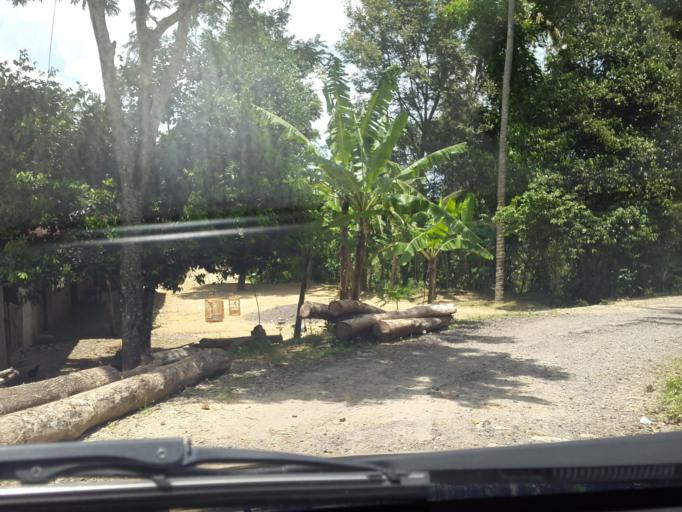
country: ID
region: Daerah Istimewa Yogyakarta
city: Wonosari
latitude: -7.8995
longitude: 110.7451
